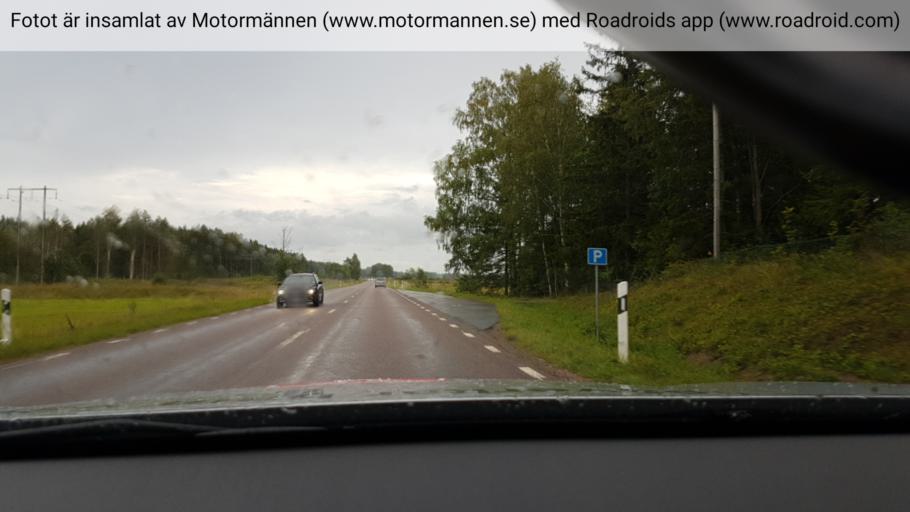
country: SE
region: Uppsala
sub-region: Tierps Kommun
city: Karlholmsbruk
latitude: 60.5016
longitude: 17.6717
